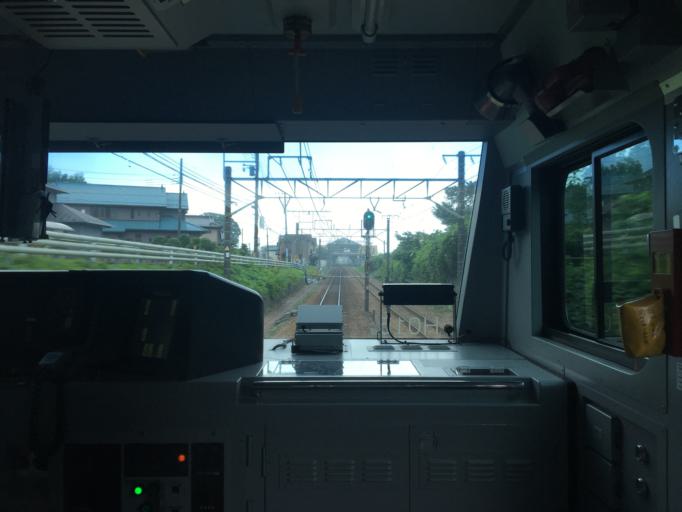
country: JP
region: Tokyo
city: Hachioji
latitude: 35.6085
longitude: 139.3320
